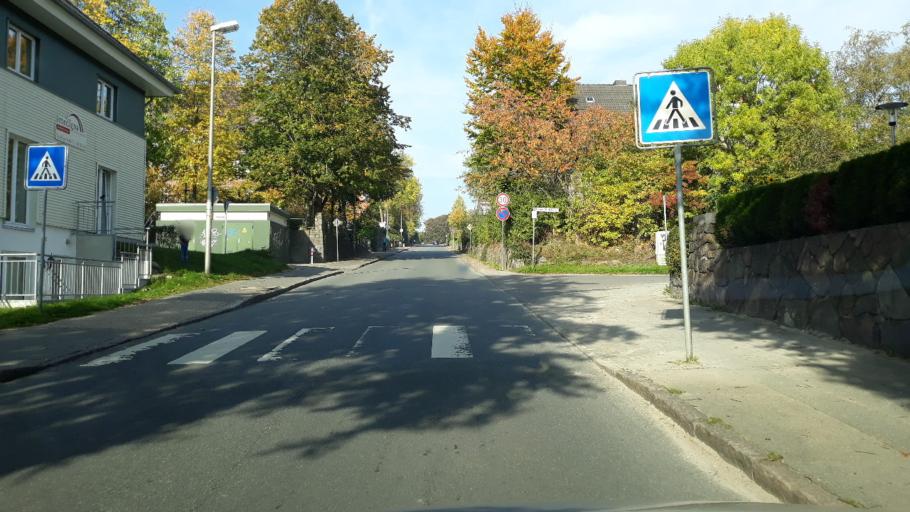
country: DE
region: Schleswig-Holstein
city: Schleswig
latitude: 54.5187
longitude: 9.5707
